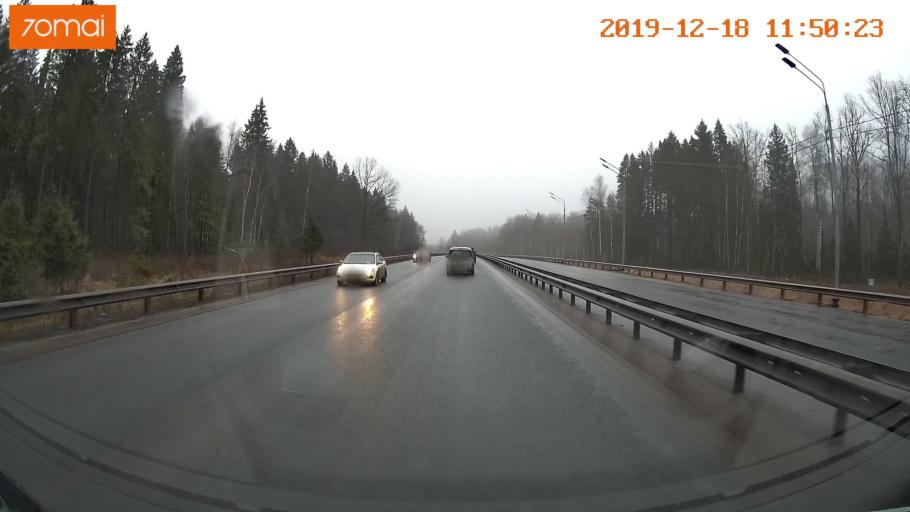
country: RU
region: Moskovskaya
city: Yershovo
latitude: 55.7854
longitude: 36.9184
